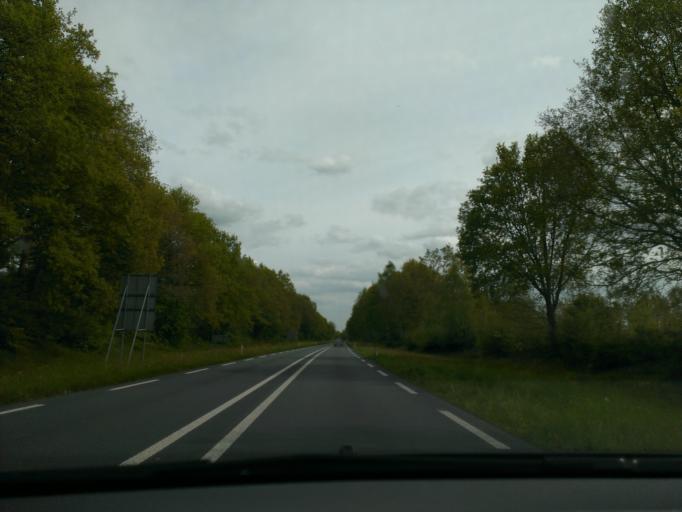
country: NL
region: Gelderland
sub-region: Gemeente Epe
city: Epe
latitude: 52.3466
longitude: 5.9653
